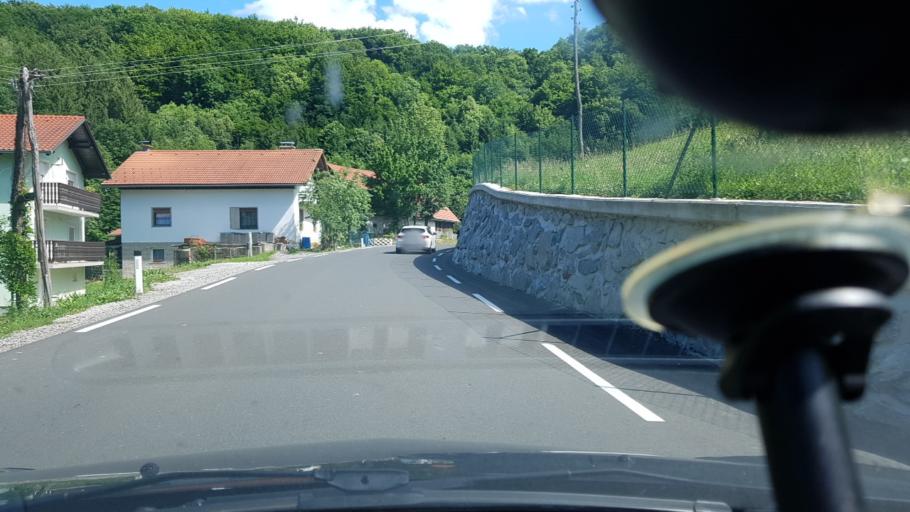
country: SI
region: Zetale
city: Zetale
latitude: 46.2824
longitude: 15.8083
